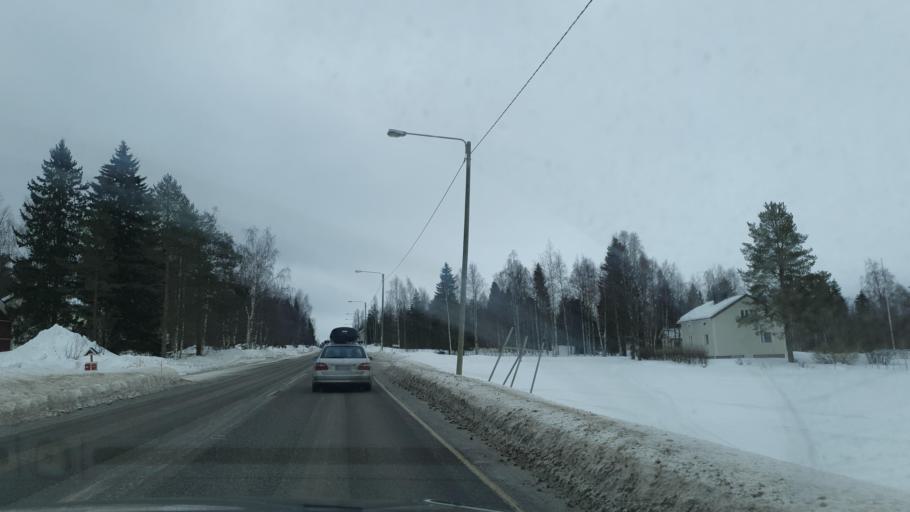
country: FI
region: Lapland
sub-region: Kemi-Tornio
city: Tornio
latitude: 66.0446
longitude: 24.0139
